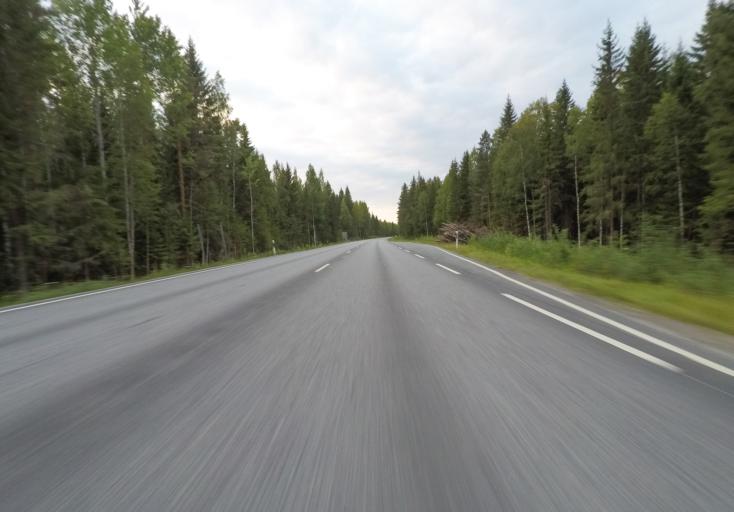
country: FI
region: Central Finland
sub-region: Jyvaeskylae
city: Toivakka
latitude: 62.2035
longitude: 26.2124
